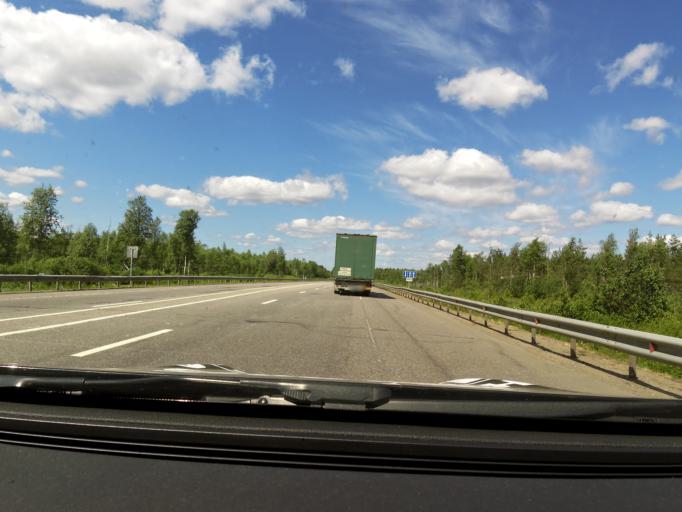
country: RU
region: Tverskaya
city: Kuzhenkino
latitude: 57.7768
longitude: 33.9188
